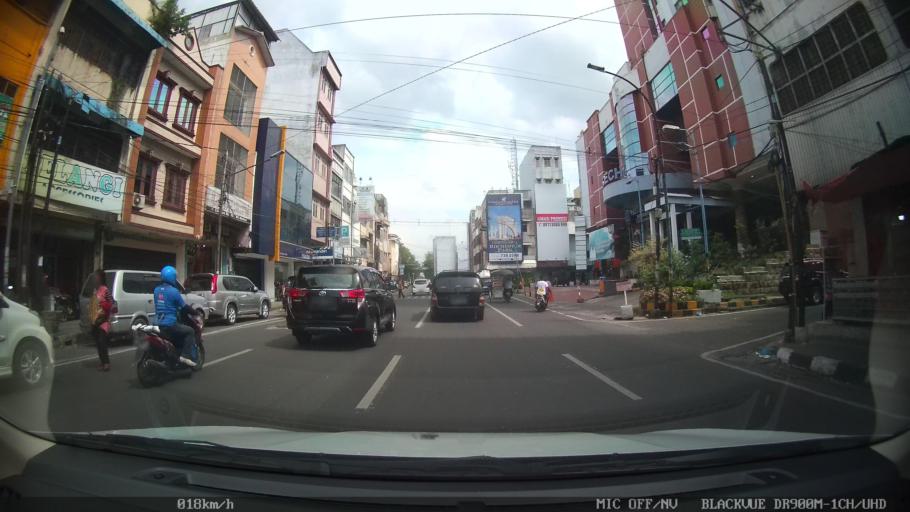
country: ID
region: North Sumatra
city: Medan
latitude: 3.5841
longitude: 98.6841
